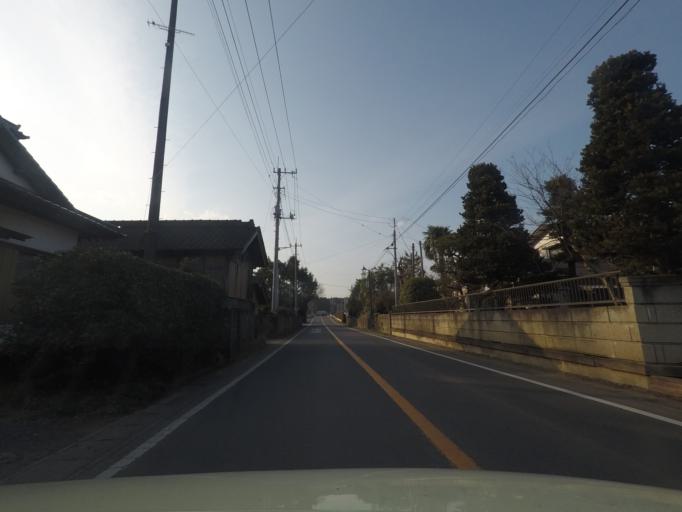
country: JP
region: Ibaraki
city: Okunoya
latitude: 36.2698
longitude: 140.4411
